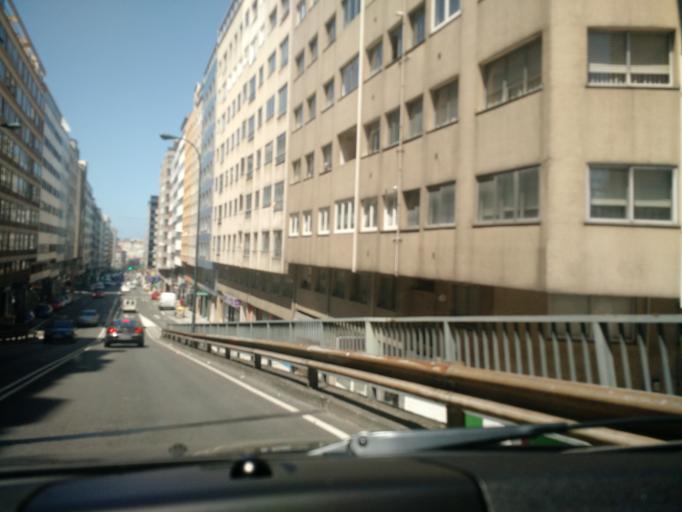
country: ES
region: Galicia
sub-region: Provincia da Coruna
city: A Coruna
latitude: 43.3617
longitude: -8.4157
